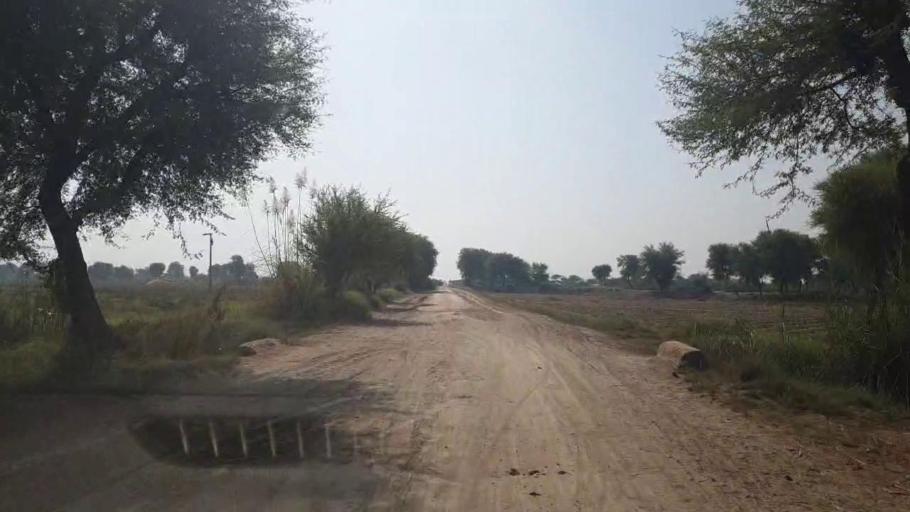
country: PK
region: Sindh
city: Shahdadpur
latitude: 25.9093
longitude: 68.7423
